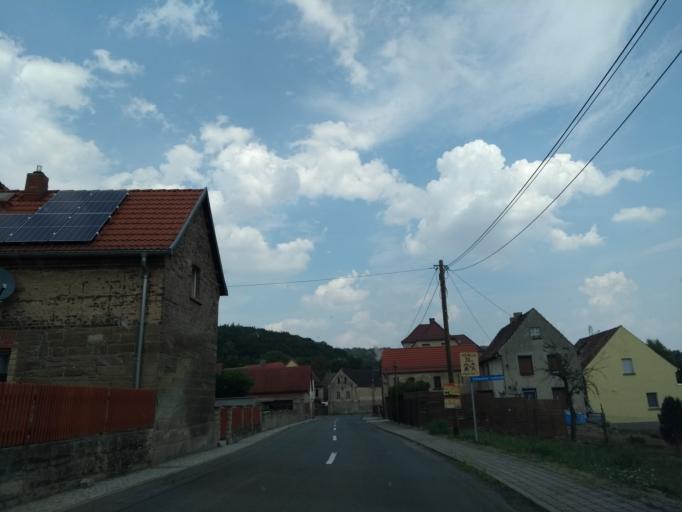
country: DE
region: Saxony-Anhalt
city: Droyssig
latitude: 51.0222
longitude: 12.0452
